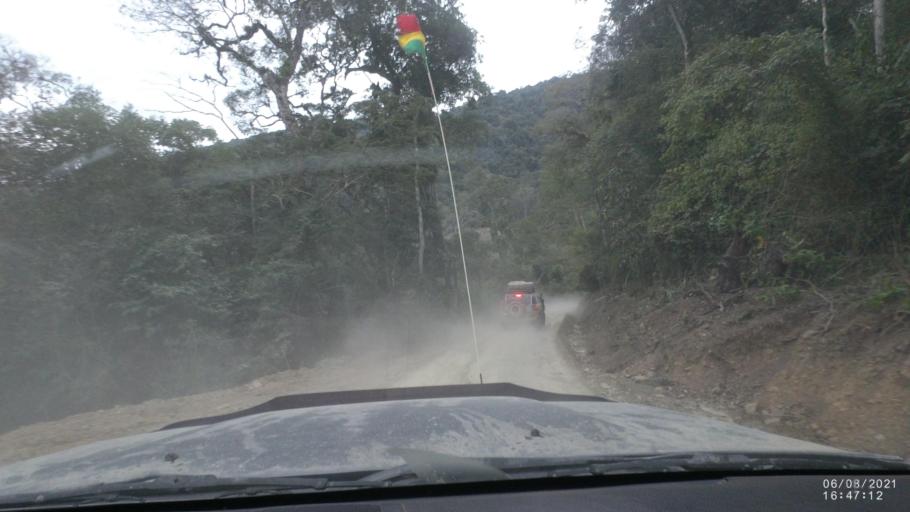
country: BO
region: La Paz
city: Quime
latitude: -16.5032
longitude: -66.7632
